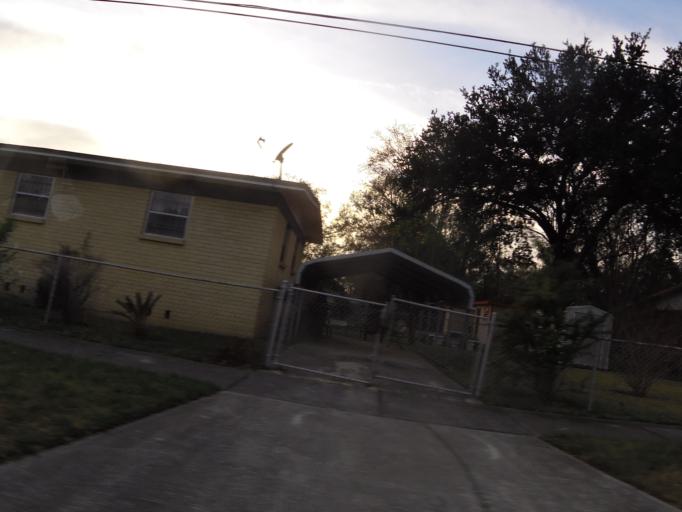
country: US
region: Florida
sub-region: Duval County
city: Jacksonville
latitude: 30.3614
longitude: -81.7051
